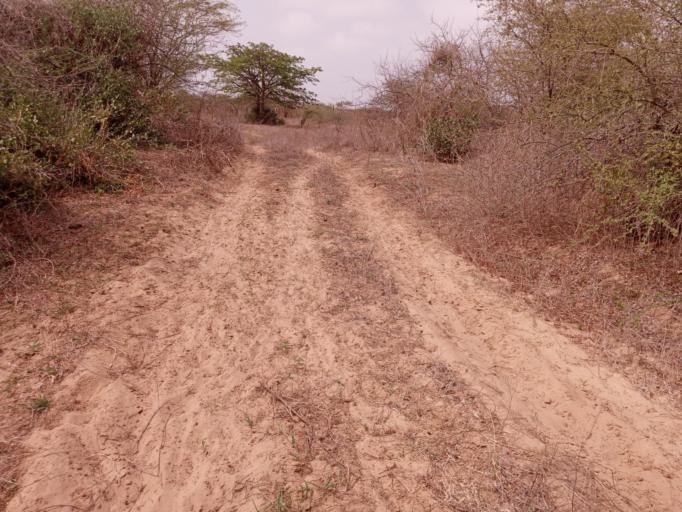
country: SN
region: Saint-Louis
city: Saint-Louis
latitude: 15.9170
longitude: -16.4536
